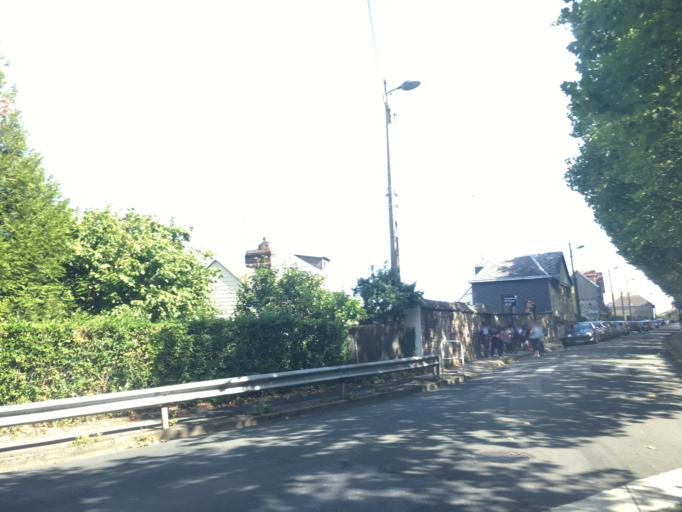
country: FR
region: Haute-Normandie
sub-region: Departement de la Seine-Maritime
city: Rouen
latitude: 49.4362
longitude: 1.1120
